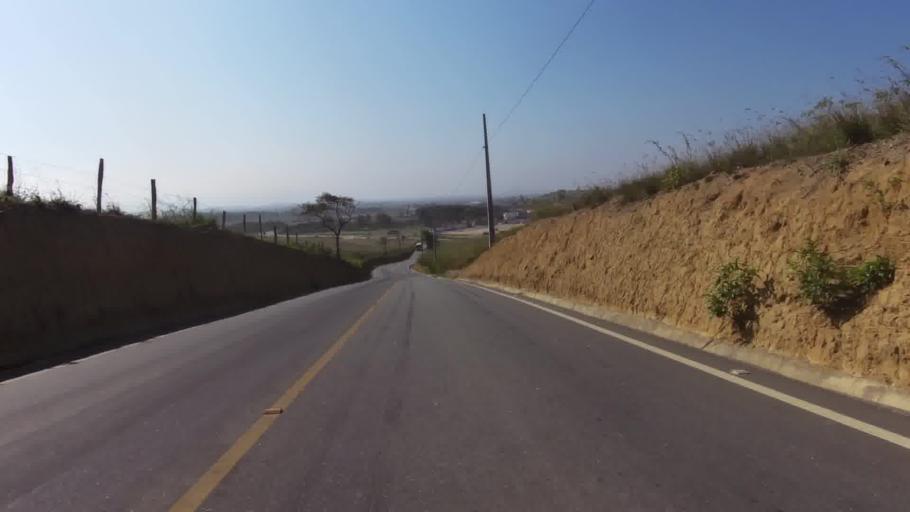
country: BR
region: Espirito Santo
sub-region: Itapemirim
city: Itapemirim
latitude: -21.0248
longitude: -40.8385
